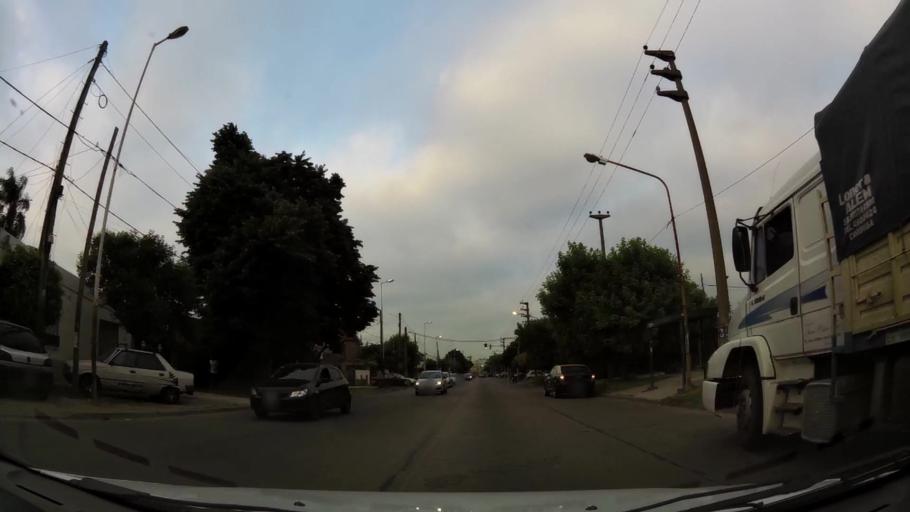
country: AR
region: Buenos Aires
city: San Justo
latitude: -34.6501
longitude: -58.5823
